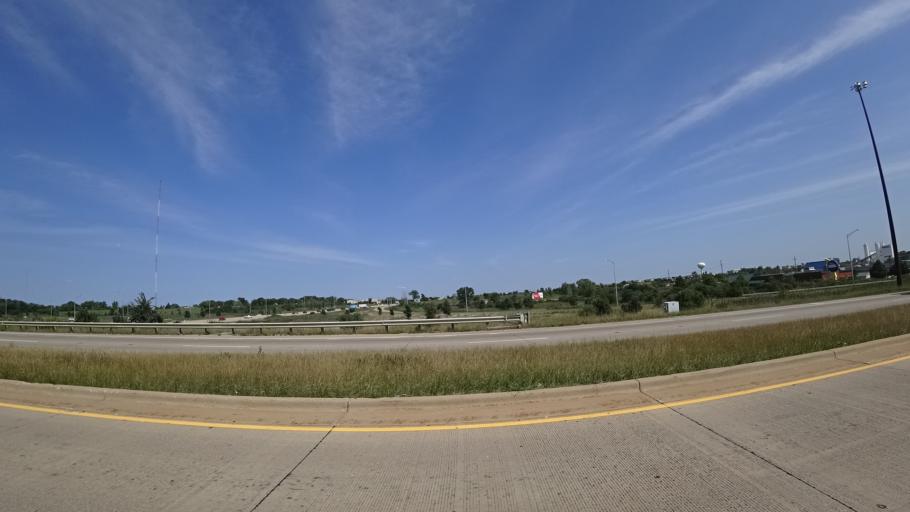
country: US
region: Illinois
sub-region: Cook County
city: Orland Hills
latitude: 41.5518
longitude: -87.8532
